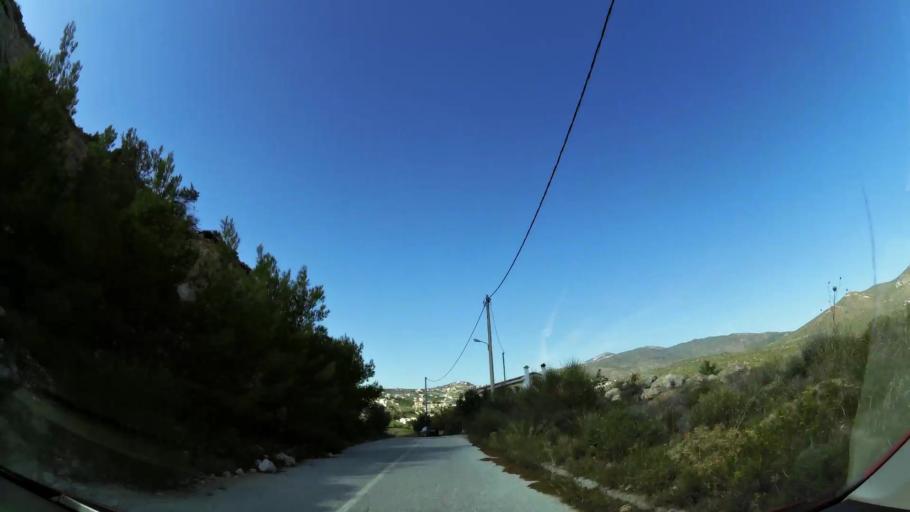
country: GR
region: Attica
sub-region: Nomarchia Anatolikis Attikis
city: Dhrafi
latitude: 38.0205
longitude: 23.9171
